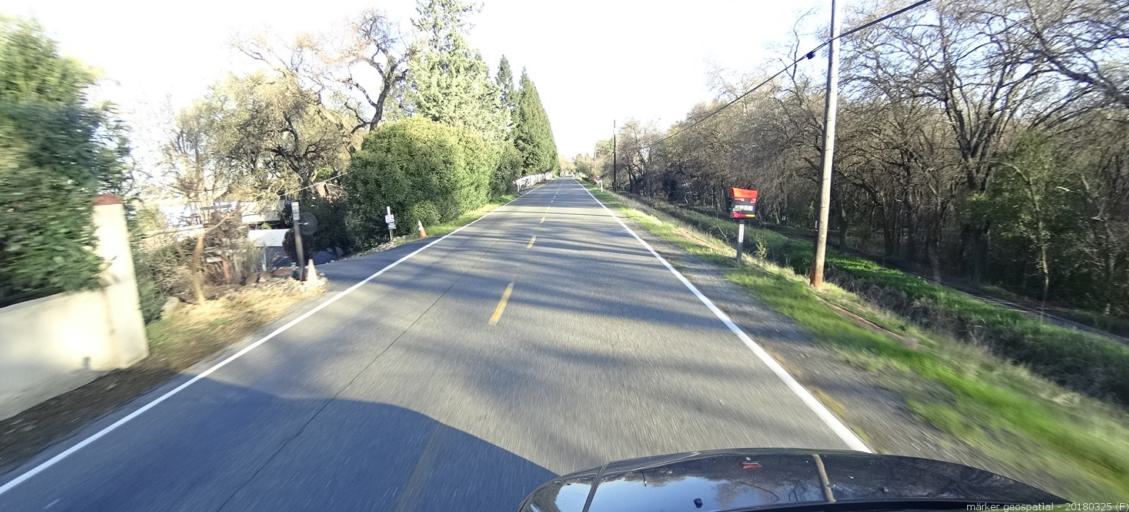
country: US
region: California
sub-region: Yolo County
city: West Sacramento
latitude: 38.6055
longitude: -121.5539
